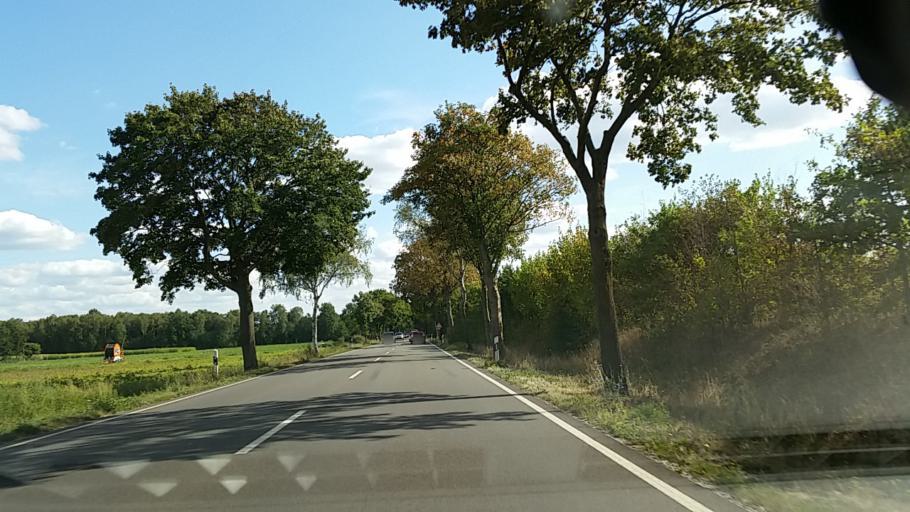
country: DE
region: Lower Saxony
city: Gross Oesingen
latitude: 52.6347
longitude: 10.4700
